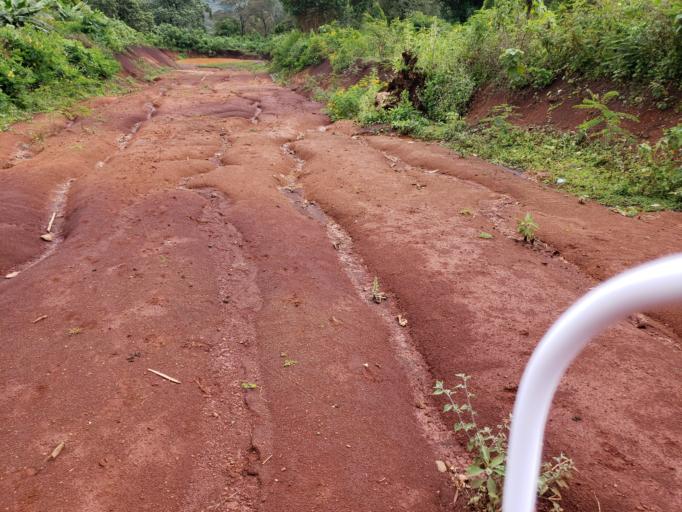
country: ET
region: Oromiya
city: Dodola
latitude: 6.4967
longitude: 39.4796
